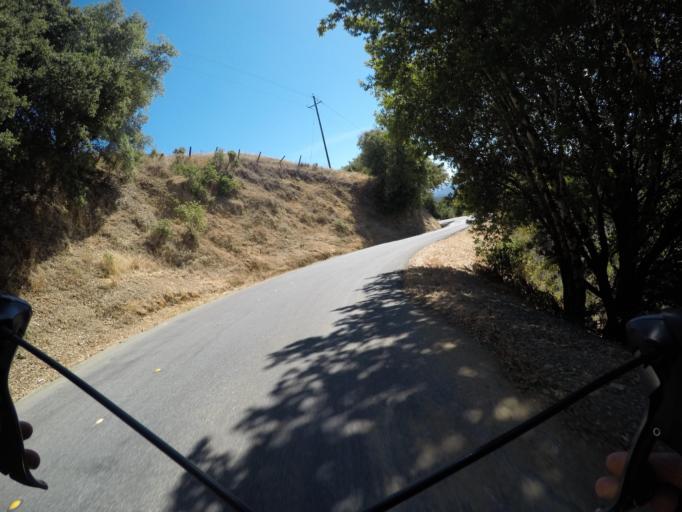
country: US
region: California
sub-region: San Mateo County
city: Portola Valley
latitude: 37.3071
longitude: -122.1976
